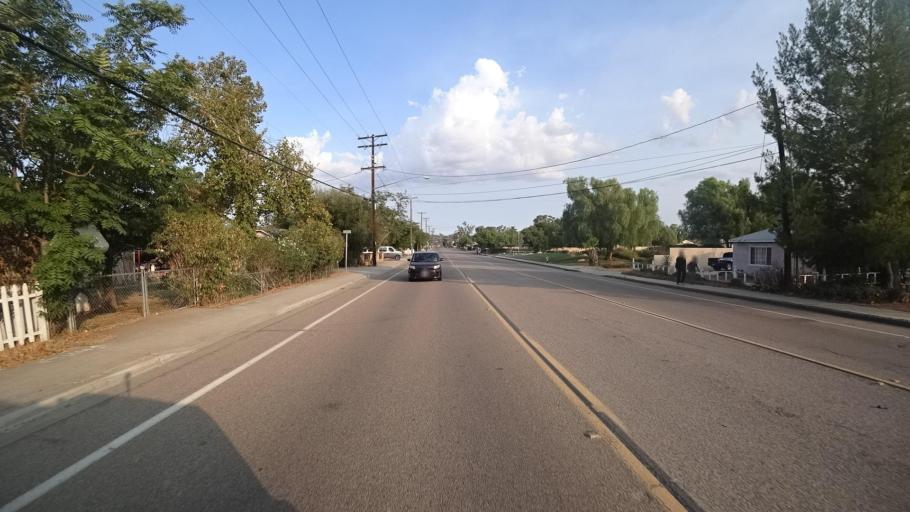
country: US
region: California
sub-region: San Diego County
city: Ramona
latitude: 33.0392
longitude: -116.8664
